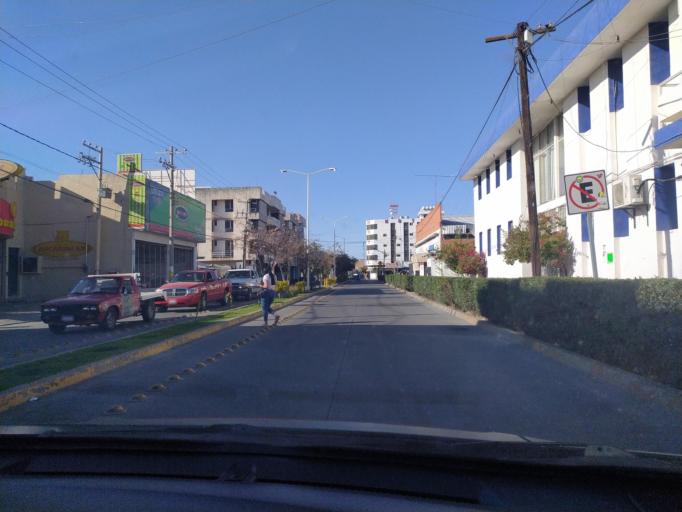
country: LA
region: Oudomxai
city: Muang La
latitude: 21.0142
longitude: 101.8591
